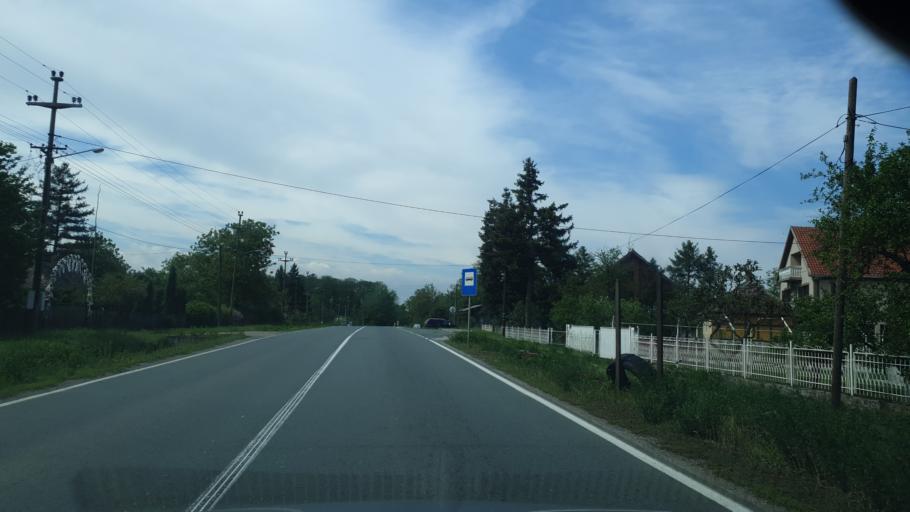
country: RS
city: Stubline
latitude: 44.5922
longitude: 20.1472
